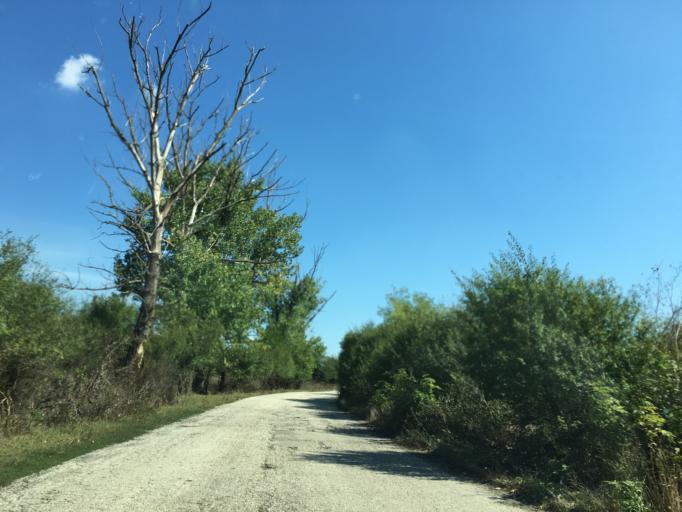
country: BG
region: Pleven
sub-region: Obshtina Knezha
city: Knezha
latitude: 43.5425
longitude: 24.1464
